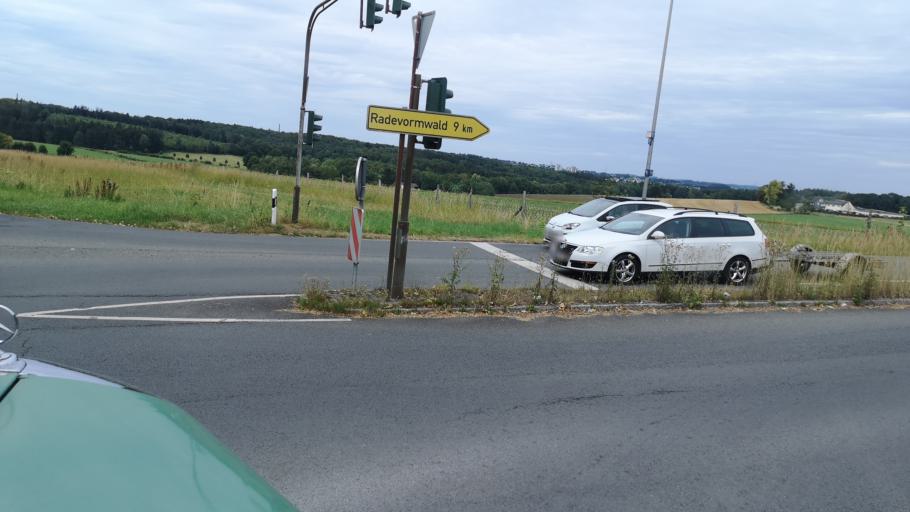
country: DE
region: North Rhine-Westphalia
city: Wermelskirchen
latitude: 51.1674
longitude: 7.2659
